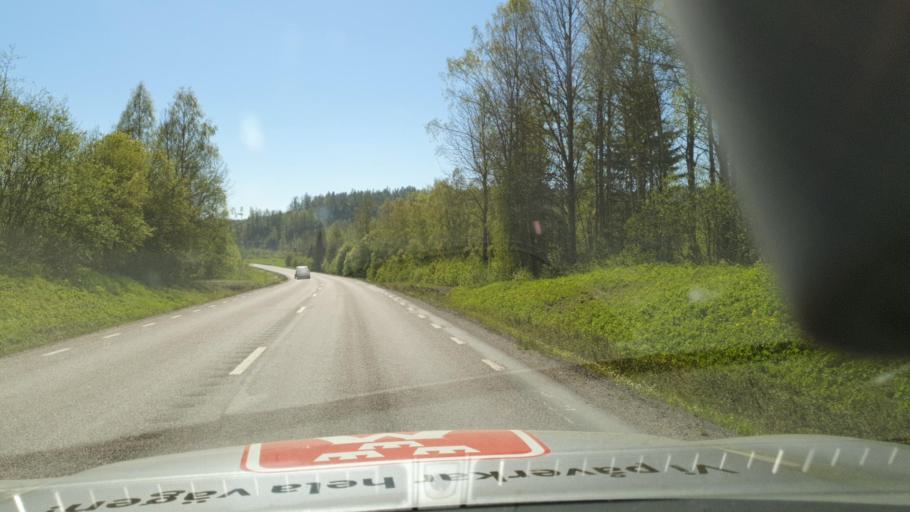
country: SE
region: Vaesternorrland
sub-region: OErnskoeldsviks Kommun
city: Ornskoldsvik
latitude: 63.3693
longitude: 18.6632
